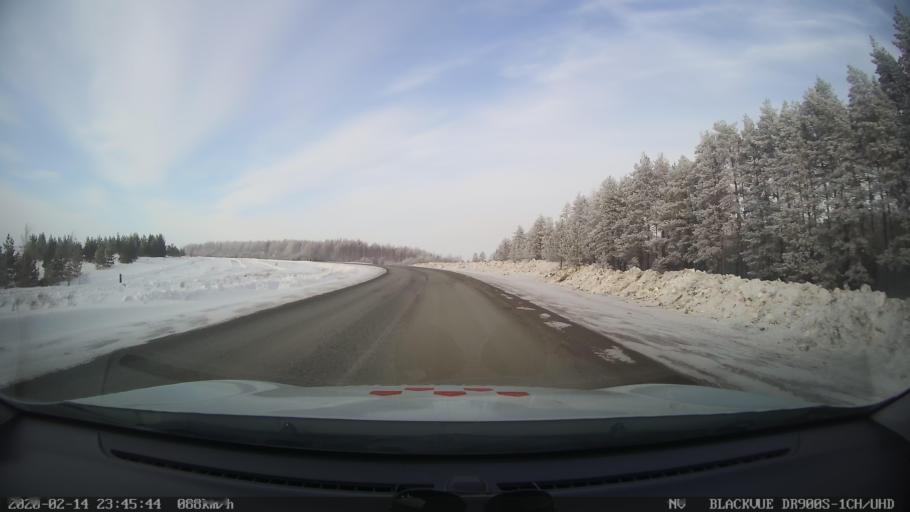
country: RU
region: Tatarstan
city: Kuybyshevskiy Zaton
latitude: 55.2243
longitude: 49.2334
